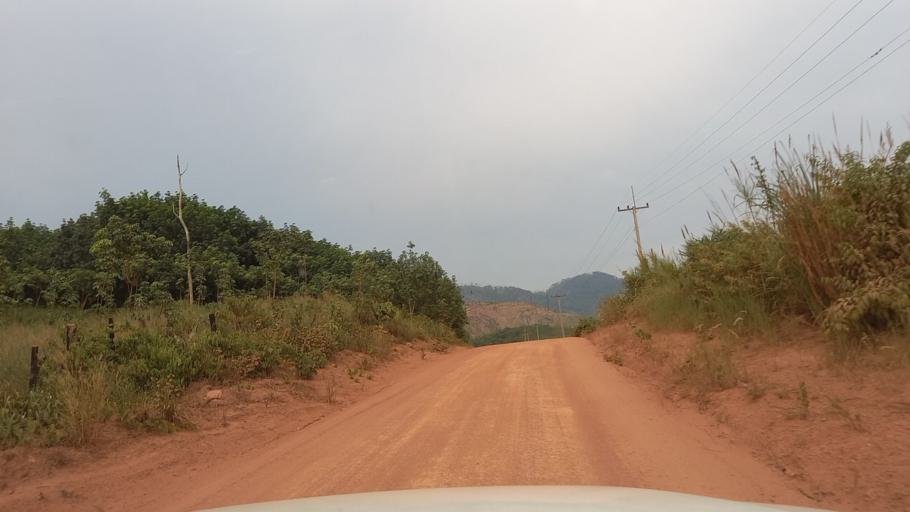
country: LA
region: Bolikhamxai
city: Bolikhan
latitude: 18.5359
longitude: 103.8138
